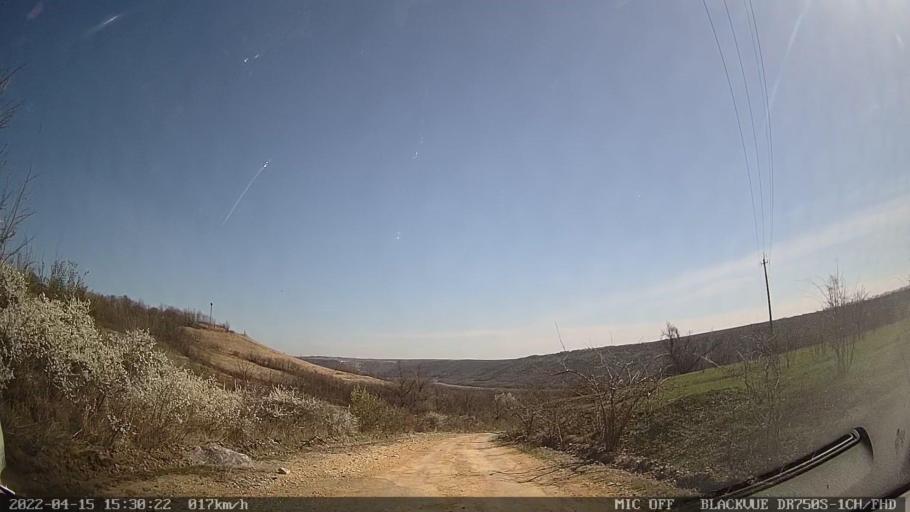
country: MD
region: Raionul Ocnita
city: Otaci
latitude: 48.3551
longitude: 27.9226
